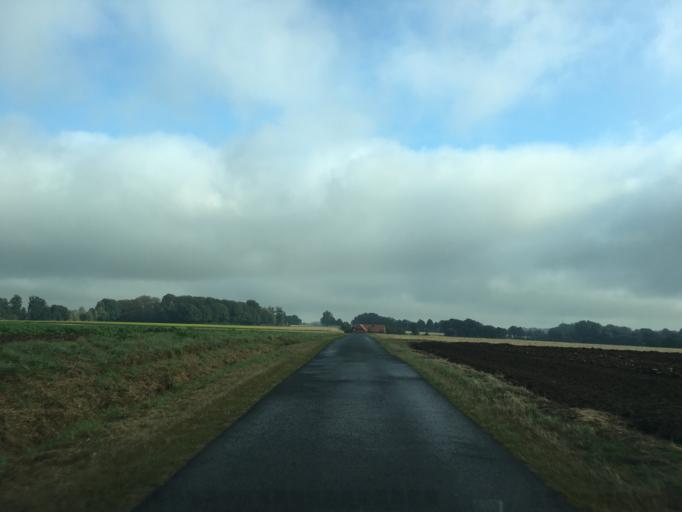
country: DE
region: North Rhine-Westphalia
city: Olfen
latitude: 51.7311
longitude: 7.3649
